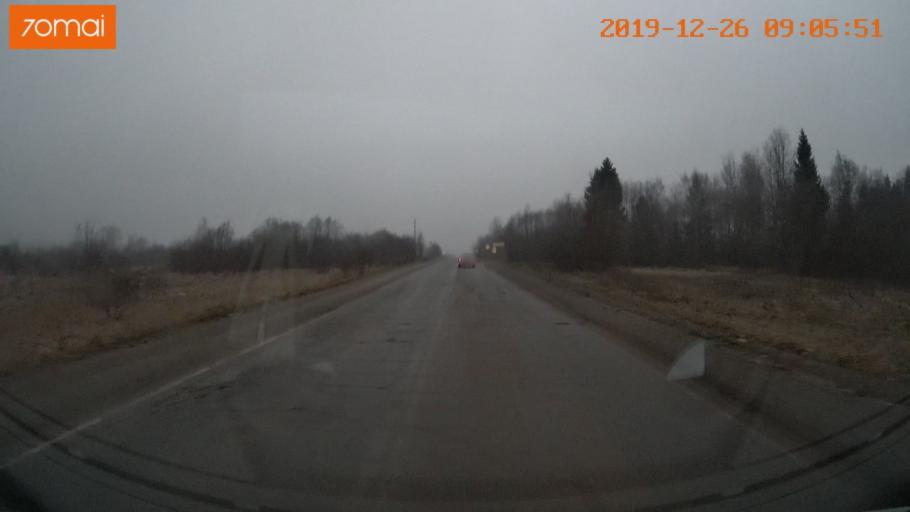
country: RU
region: Vologda
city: Gryazovets
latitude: 58.8300
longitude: 40.2555
